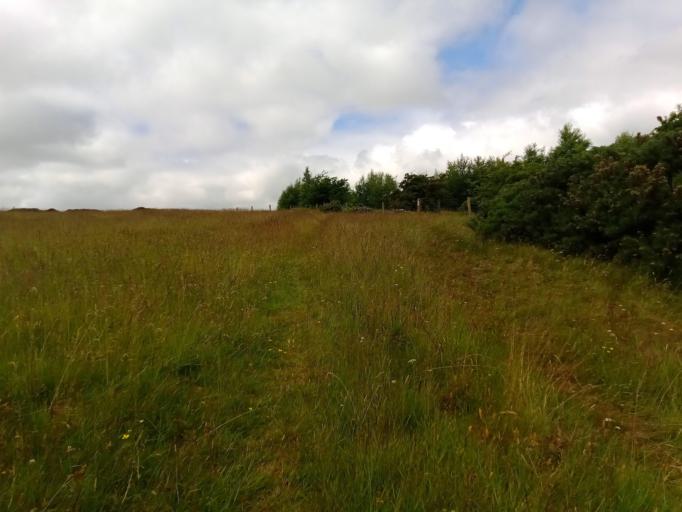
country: IE
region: Leinster
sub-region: Laois
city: Rathdowney
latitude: 52.7997
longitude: -7.4710
